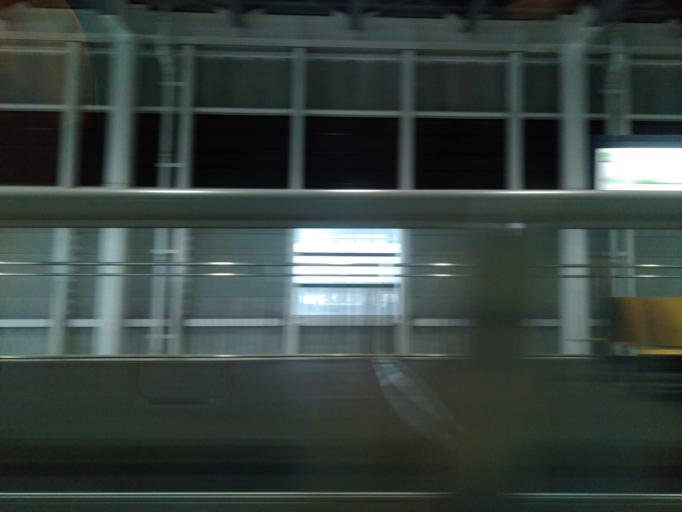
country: JP
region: Hokkaido
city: Nanae
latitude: 41.9044
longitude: 140.6496
